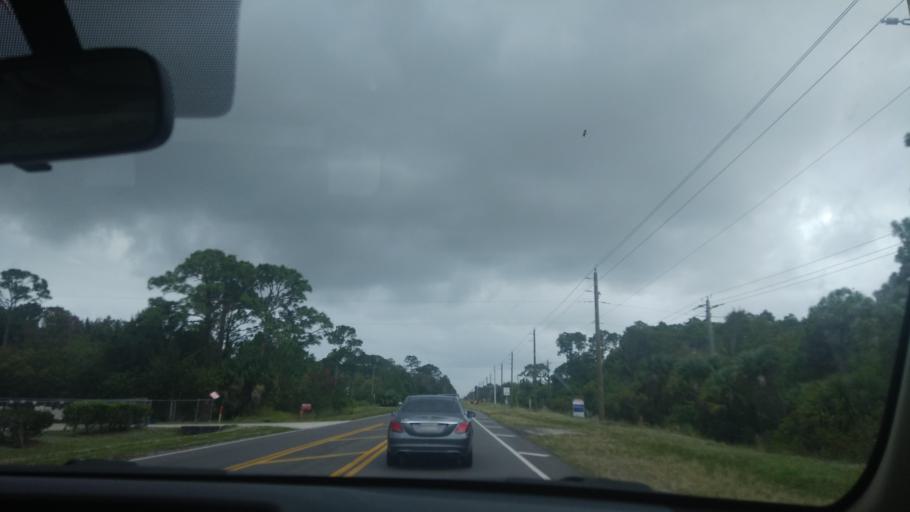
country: US
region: Florida
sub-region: Brevard County
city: Malabar
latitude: 27.9794
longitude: -80.6225
